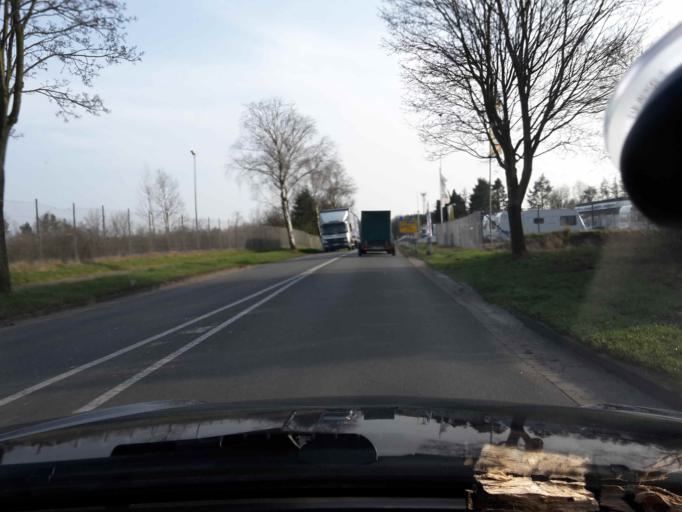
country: DE
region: Lower Saxony
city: Hollenstedt
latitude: 53.3620
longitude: 9.7110
